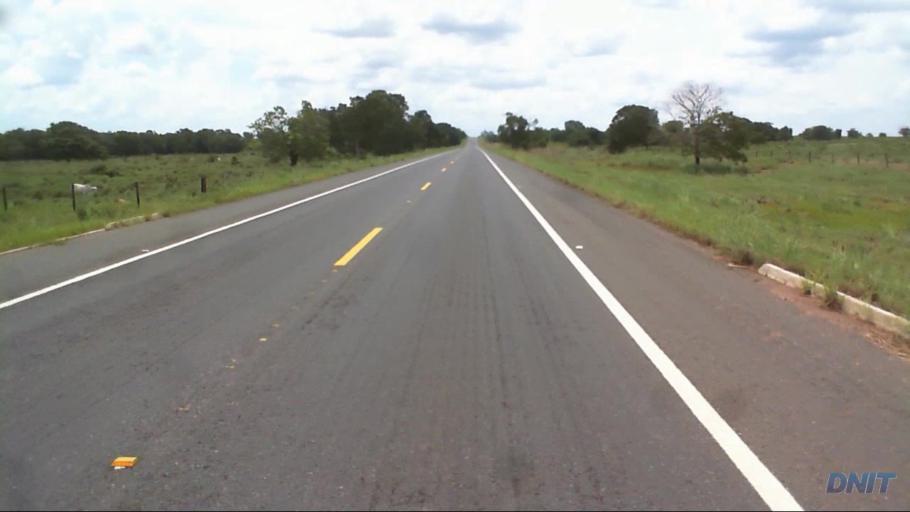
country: BR
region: Goias
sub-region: Sao Miguel Do Araguaia
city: Sao Miguel do Araguaia
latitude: -13.2912
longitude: -50.4142
